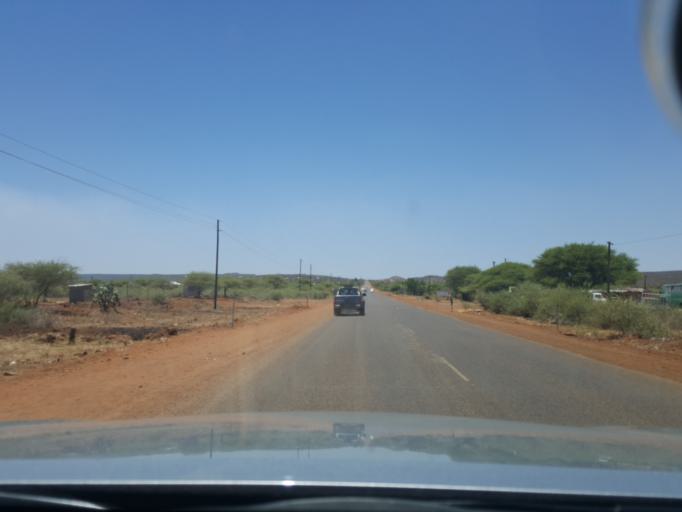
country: ZA
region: North-West
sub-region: Ngaka Modiri Molema District Municipality
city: Zeerust
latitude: -25.4328
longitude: 25.9607
